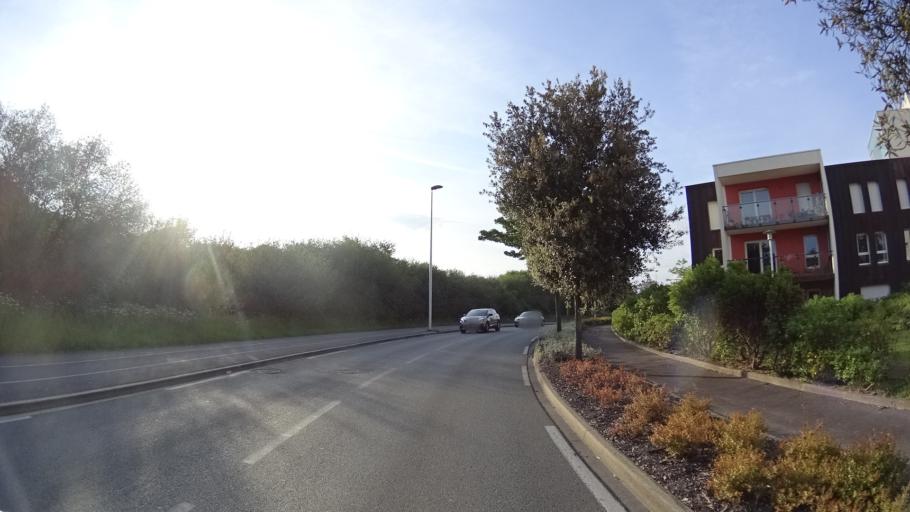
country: FR
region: Brittany
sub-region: Departement du Morbihan
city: Vannes
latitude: 47.6481
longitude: -2.7439
